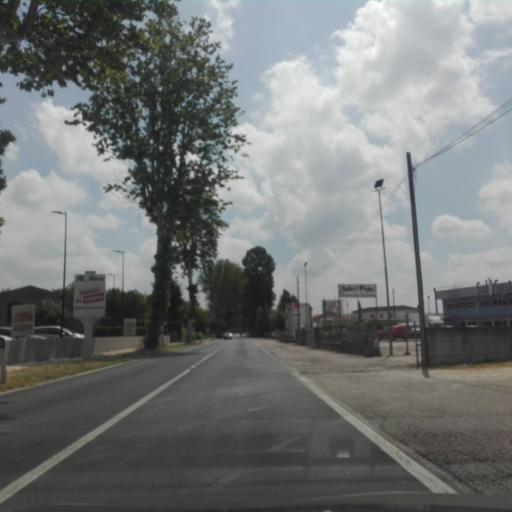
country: IT
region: Veneto
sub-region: Provincia di Rovigo
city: Villadose
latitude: 45.0690
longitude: 11.8890
